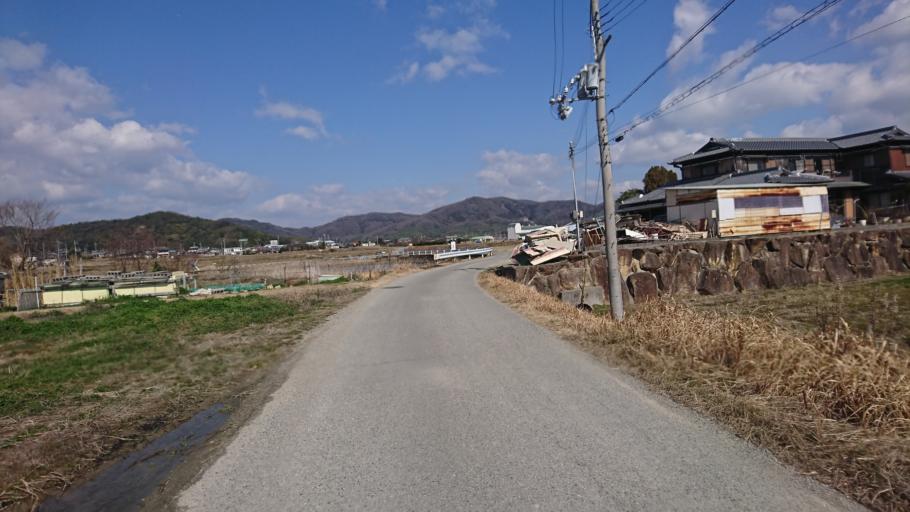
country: JP
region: Hyogo
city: Kakogawacho-honmachi
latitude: 34.8075
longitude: 134.8061
